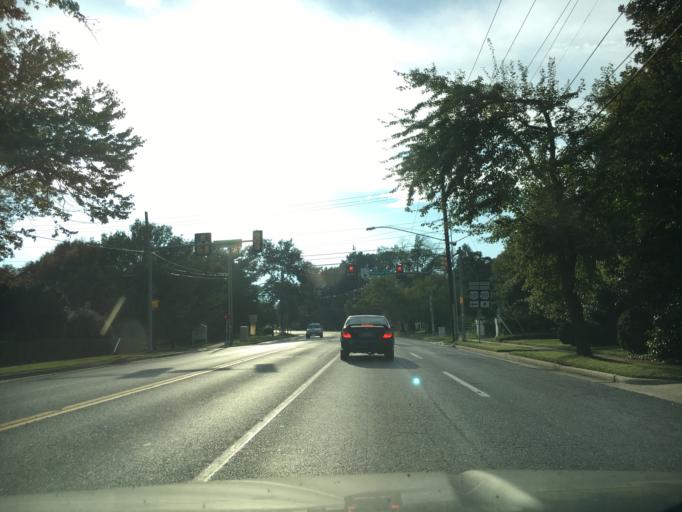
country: US
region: Virginia
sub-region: City of Lynchburg
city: West Lynchburg
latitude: 37.4395
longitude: -79.1845
